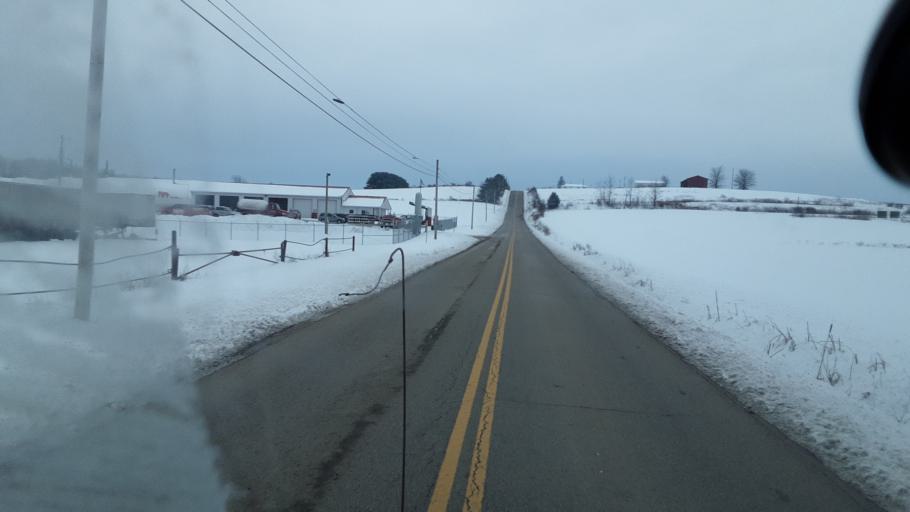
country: US
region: Ohio
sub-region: Perry County
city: Somerset
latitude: 39.9348
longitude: -82.2237
